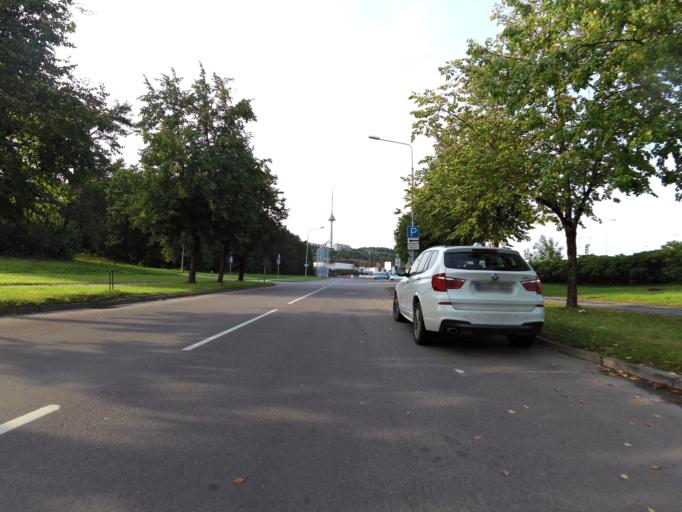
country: LT
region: Vilnius County
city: Lazdynai
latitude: 54.6762
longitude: 25.2264
